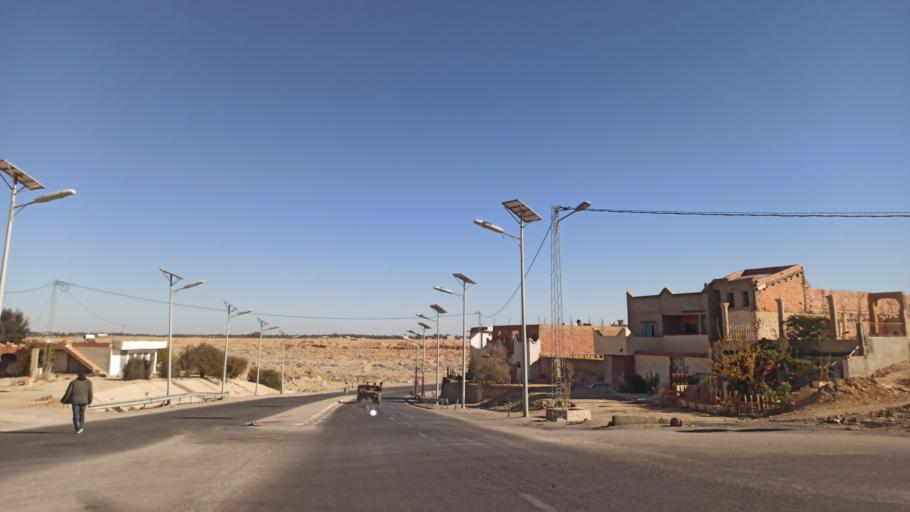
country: TN
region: Gafsa
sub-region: Gafsa Municipality
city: Gafsa
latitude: 34.4336
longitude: 8.7995
